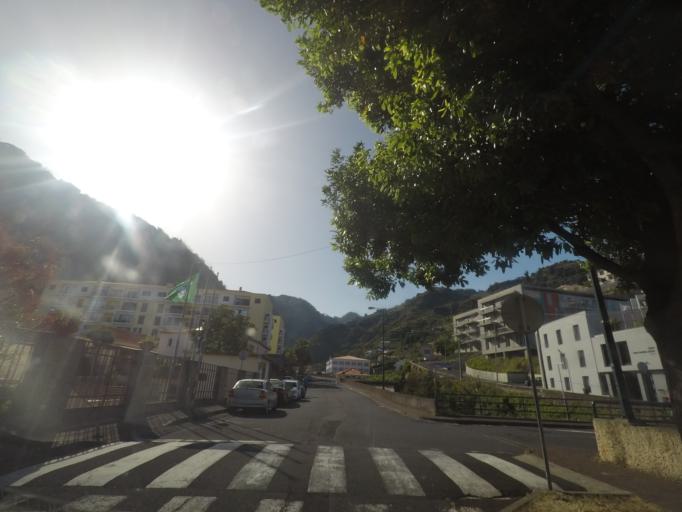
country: PT
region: Madeira
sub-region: Santa Cruz
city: Santa Cruz
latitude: 32.6892
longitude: -16.7954
